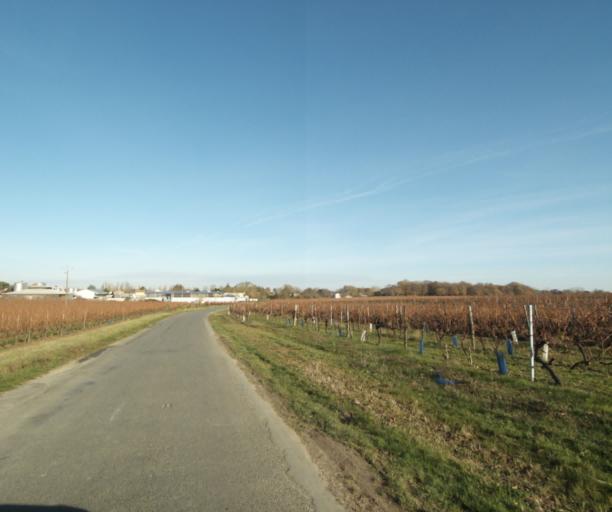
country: FR
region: Poitou-Charentes
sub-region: Departement de la Charente-Maritime
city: Burie
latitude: 45.7696
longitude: -0.4180
